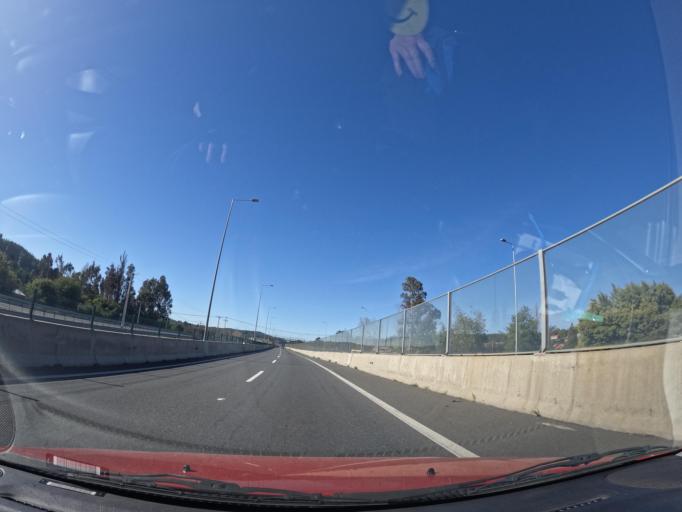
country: CL
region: Biobio
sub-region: Provincia de Biobio
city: Yumbel
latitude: -36.9857
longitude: -72.6260
